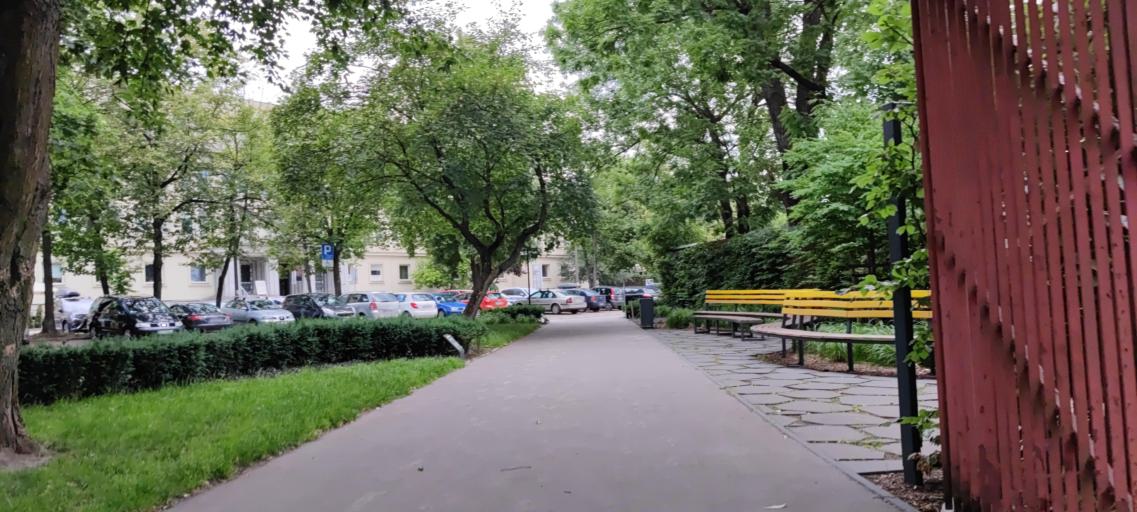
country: PL
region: Lesser Poland Voivodeship
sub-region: Krakow
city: Krakow
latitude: 50.0572
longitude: 19.9188
